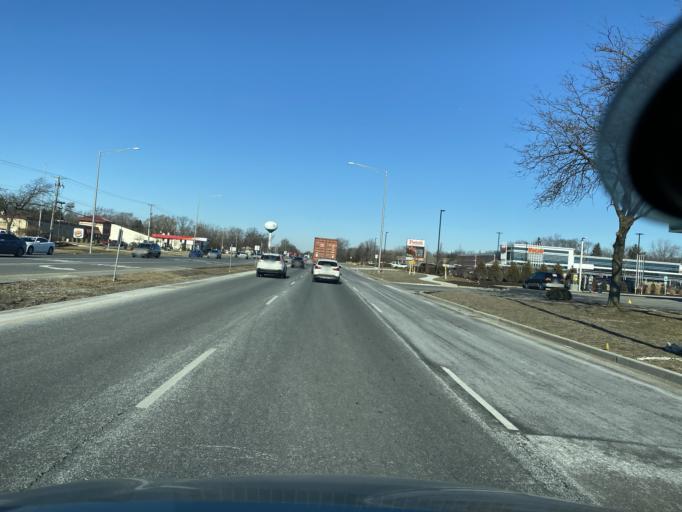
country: US
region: Illinois
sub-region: DuPage County
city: Willowbrook
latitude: 41.7612
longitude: -87.9448
